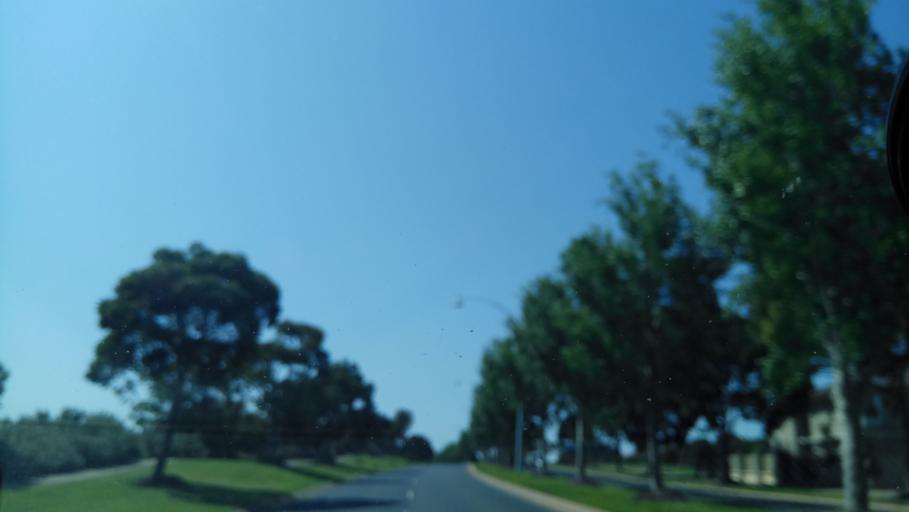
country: AU
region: Victoria
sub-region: Hobsons Bay
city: Altona Meadows
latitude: -37.8917
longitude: 144.7612
